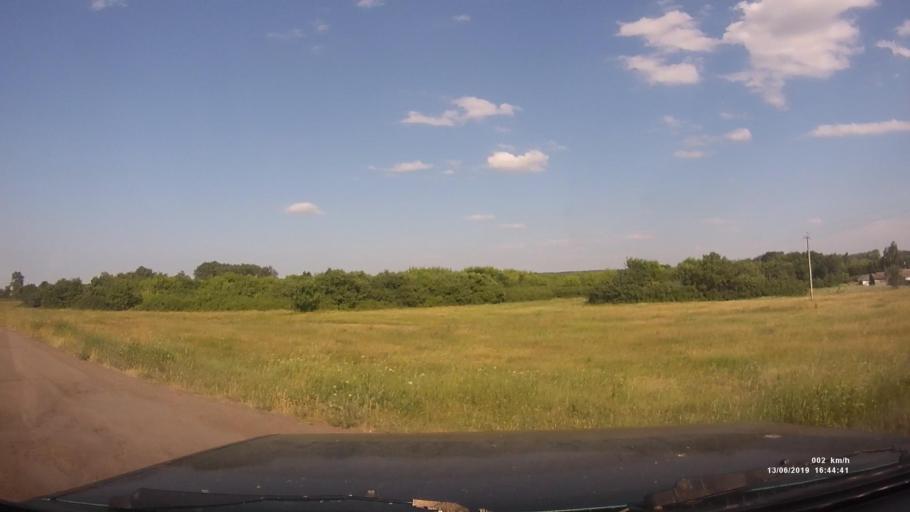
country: RU
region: Rostov
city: Kazanskaya
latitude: 49.9458
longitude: 41.4213
